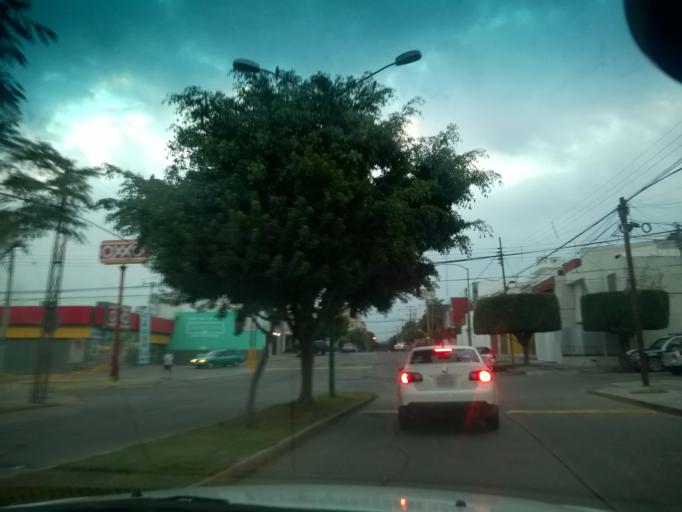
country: MX
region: Guanajuato
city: Leon
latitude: 21.1507
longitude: -101.6964
